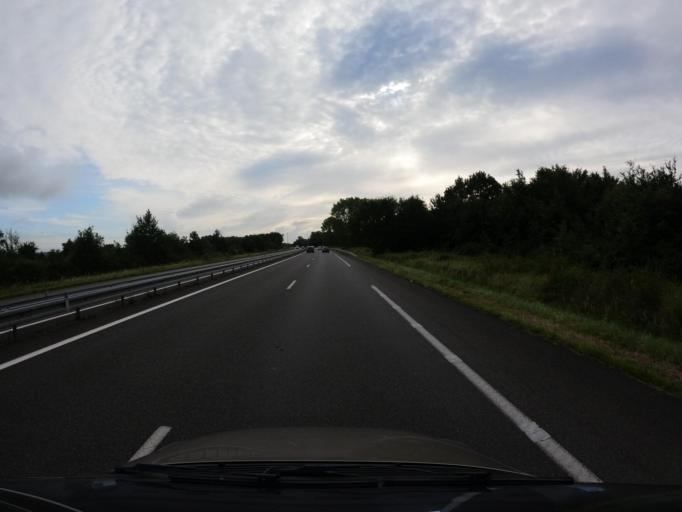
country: FR
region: Centre
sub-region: Departement d'Indre-et-Loire
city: Restigne
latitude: 47.2653
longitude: 0.2370
